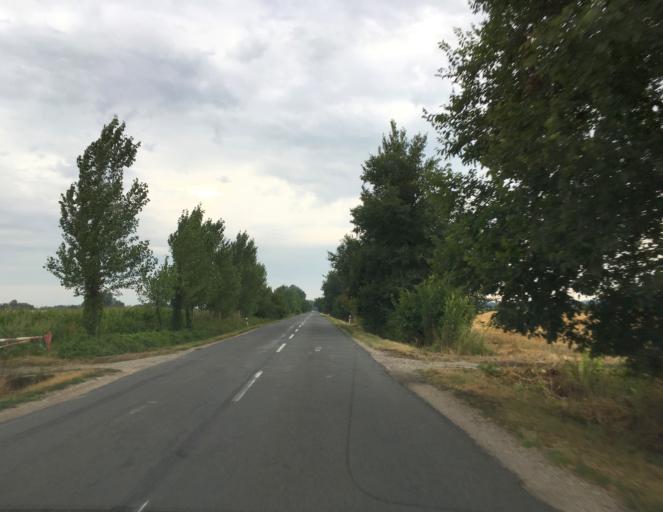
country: SK
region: Trnavsky
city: Gabcikovo
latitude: 47.8950
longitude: 17.6751
